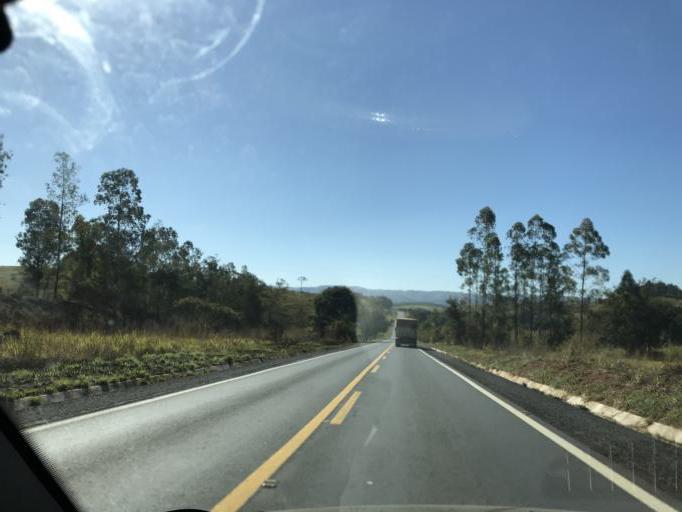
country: BR
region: Minas Gerais
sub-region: Bambui
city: Bambui
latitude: -19.8649
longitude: -45.9856
